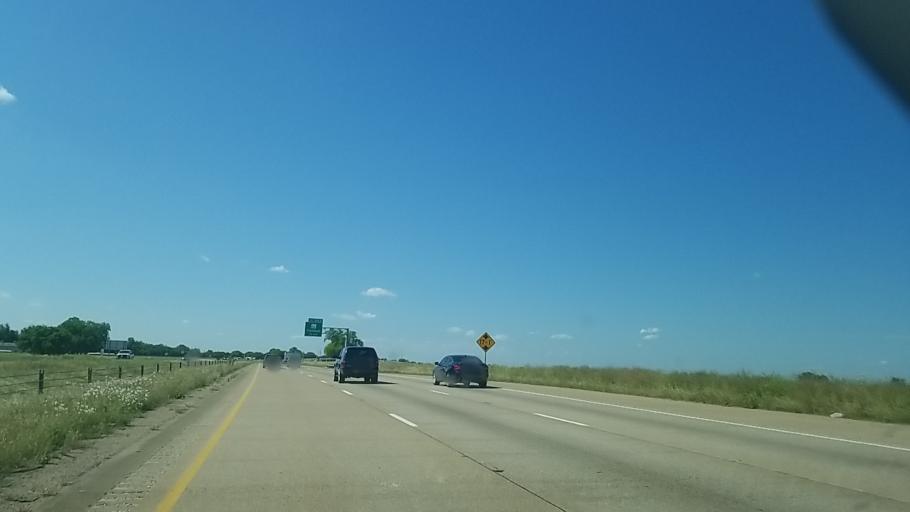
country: US
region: Texas
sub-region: Ellis County
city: Palmer
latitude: 32.4765
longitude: -96.6618
